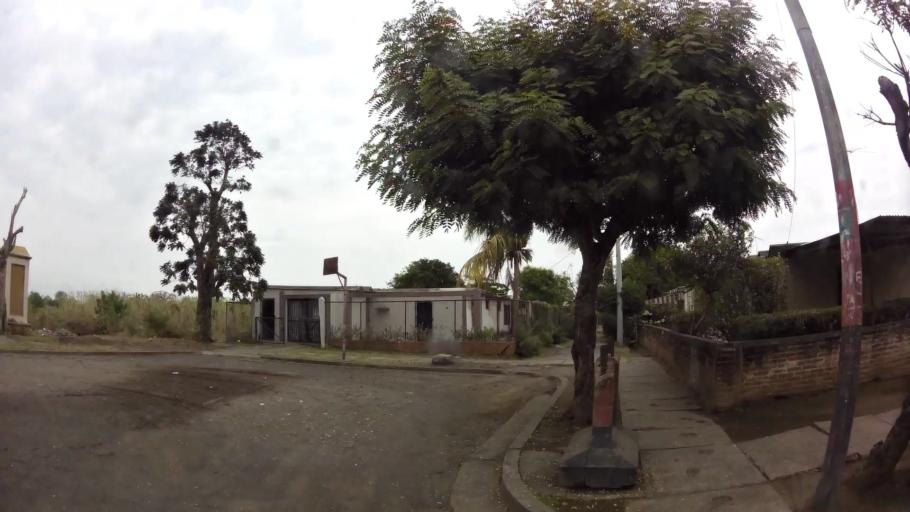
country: NI
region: Granada
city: Granada
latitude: 11.9483
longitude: -85.9512
